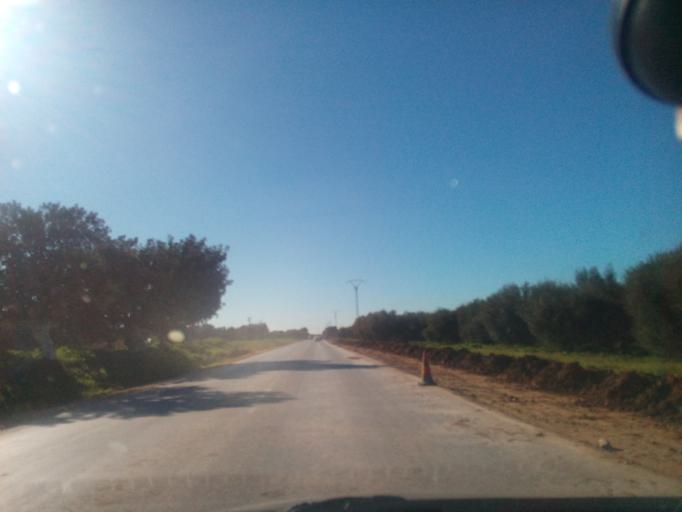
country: DZ
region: Relizane
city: Djidiouia
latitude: 35.9210
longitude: 0.7958
